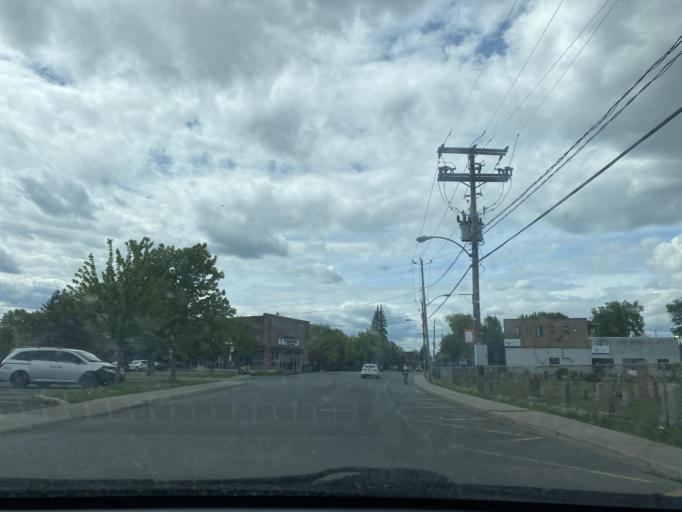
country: CA
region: Quebec
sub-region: Monteregie
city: Carignan
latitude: 45.4507
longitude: -73.2959
